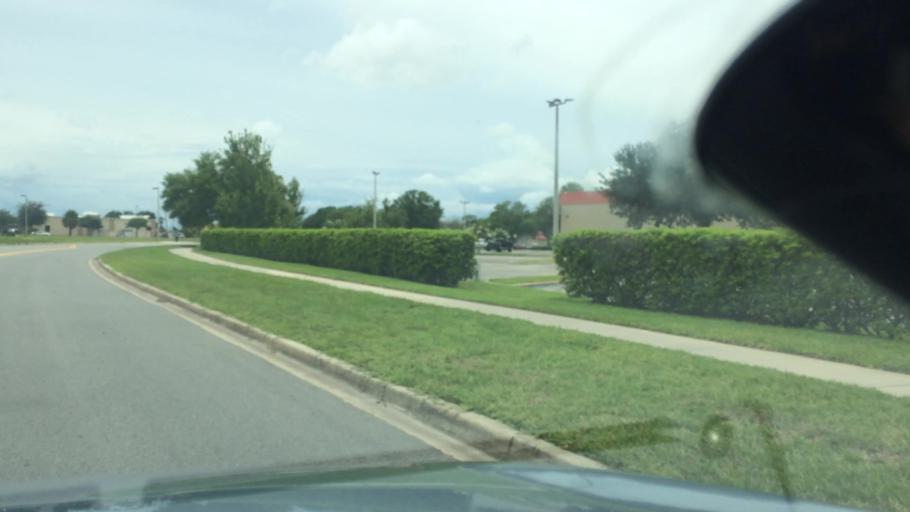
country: US
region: Florida
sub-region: Osceola County
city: Kissimmee
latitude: 28.3075
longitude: -81.4404
